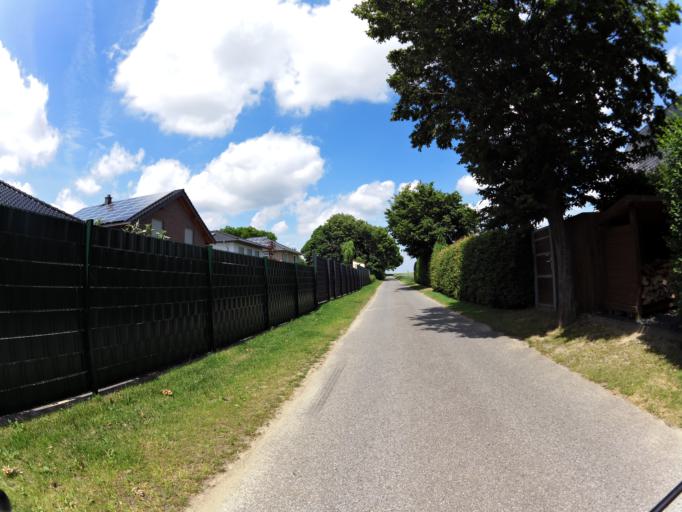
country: NL
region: Limburg
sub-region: Gemeente Echt-Susteren
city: Koningsbosch
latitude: 51.0296
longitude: 5.9865
